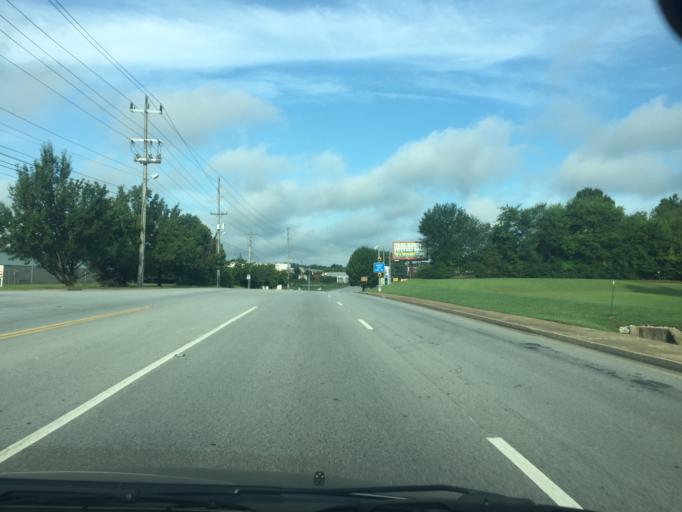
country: US
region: Tennessee
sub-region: Hamilton County
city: East Chattanooga
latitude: 35.0737
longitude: -85.1878
